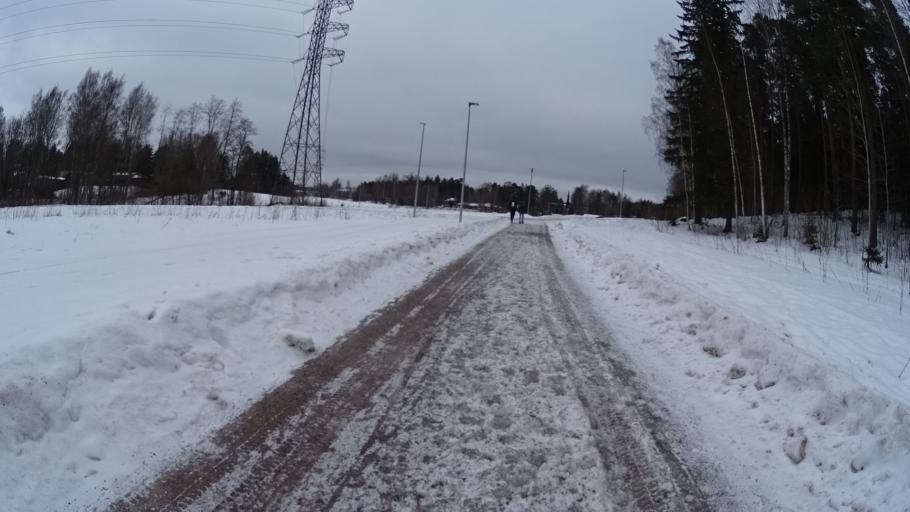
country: FI
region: Uusimaa
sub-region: Helsinki
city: Kilo
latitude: 60.2100
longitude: 24.7803
